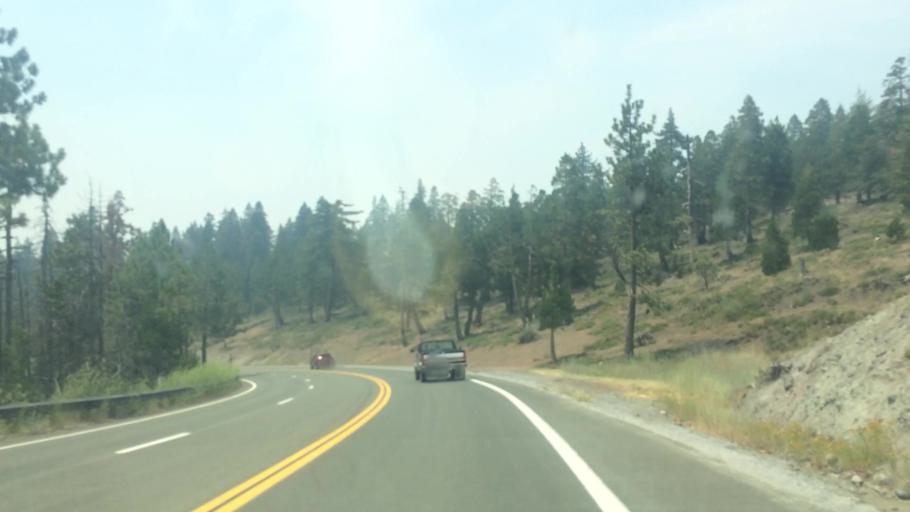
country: US
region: California
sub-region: Amador County
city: Pioneer
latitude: 38.5454
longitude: -120.3134
